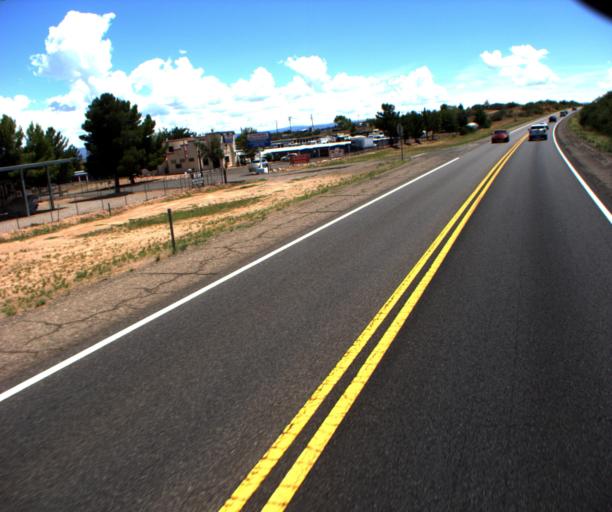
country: US
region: Arizona
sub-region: Yavapai County
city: Camp Verde
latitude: 34.6184
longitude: -111.9191
